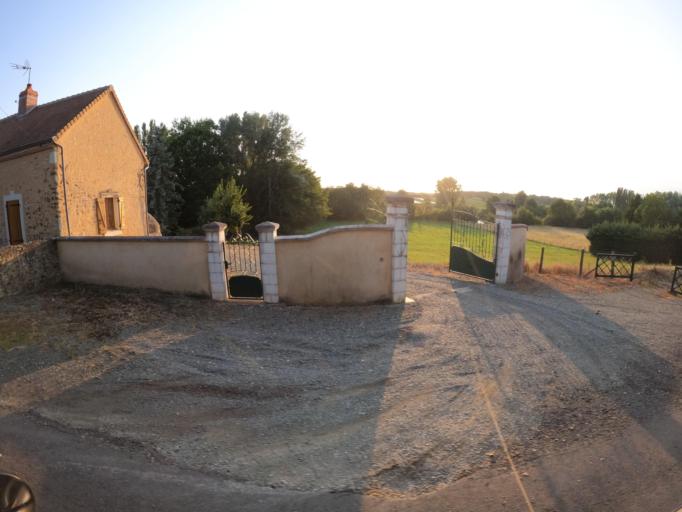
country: FR
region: Pays de la Loire
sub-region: Departement de la Sarthe
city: Parce-sur-Sarthe
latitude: 47.8475
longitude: -0.1939
